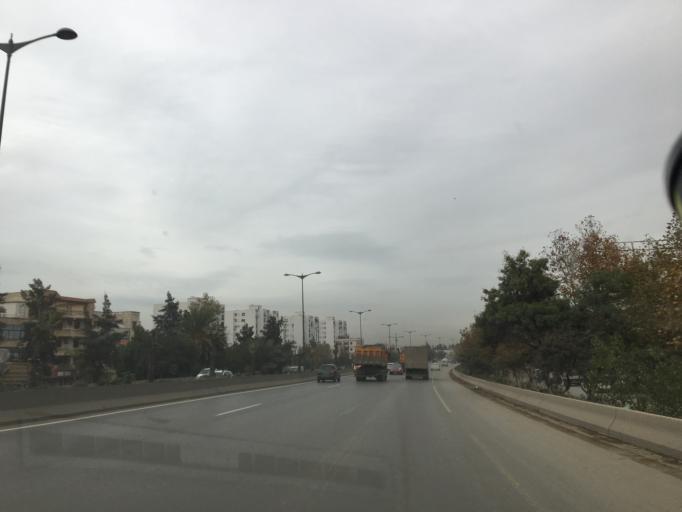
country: DZ
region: Alger
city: Dar el Beida
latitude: 36.7121
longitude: 3.2157
